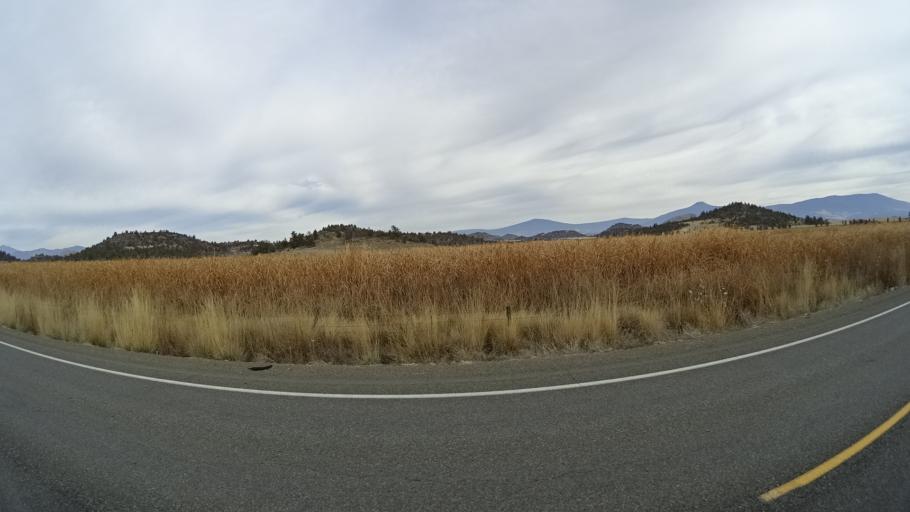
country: US
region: California
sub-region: Siskiyou County
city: Montague
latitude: 41.6439
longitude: -122.4890
